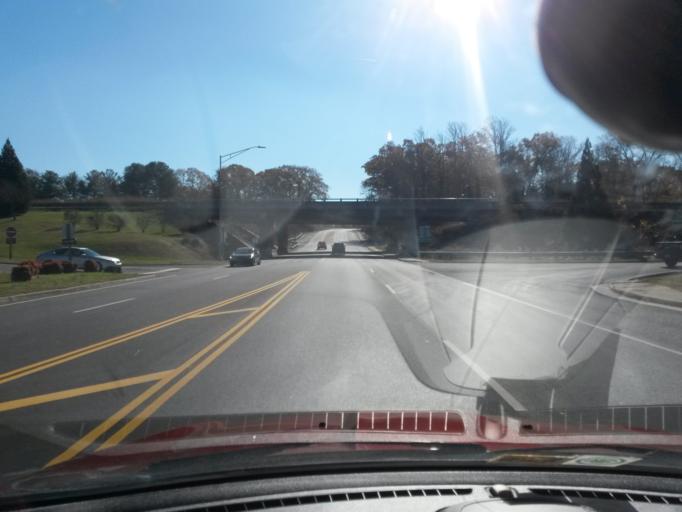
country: US
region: Virginia
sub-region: City of Bedford
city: Bedford
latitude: 37.3256
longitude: -79.5033
